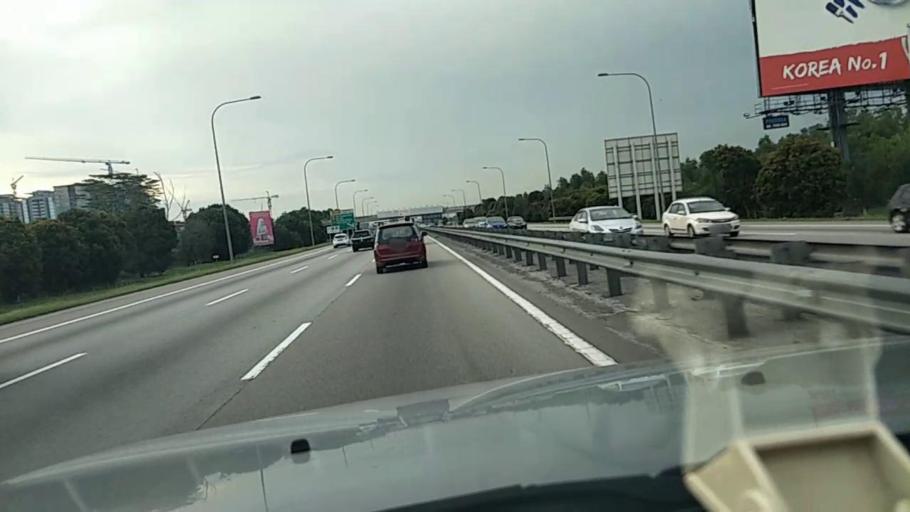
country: MY
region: Putrajaya
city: Putrajaya
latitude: 2.9395
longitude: 101.5953
